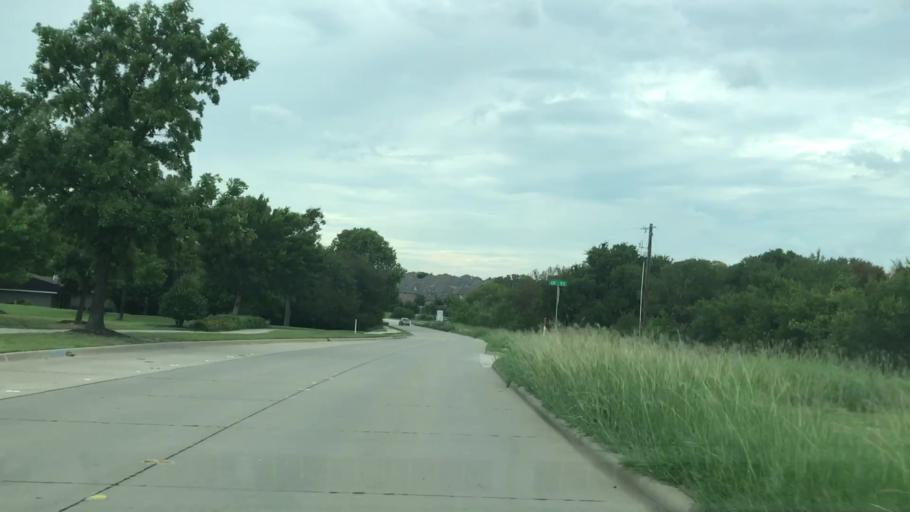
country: US
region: Texas
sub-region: Collin County
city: Prosper
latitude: 33.1884
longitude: -96.7870
